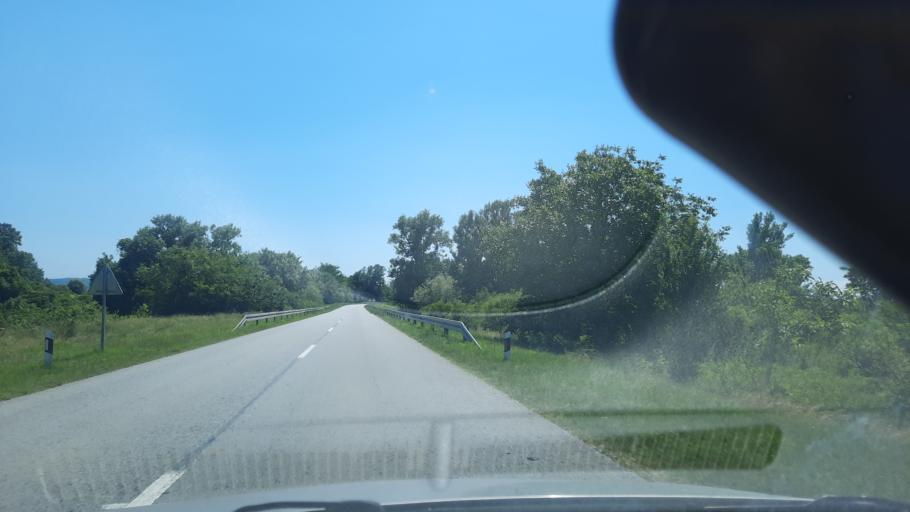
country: RO
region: Caras-Severin
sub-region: Comuna Socol
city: Socol
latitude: 44.8608
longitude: 21.3071
